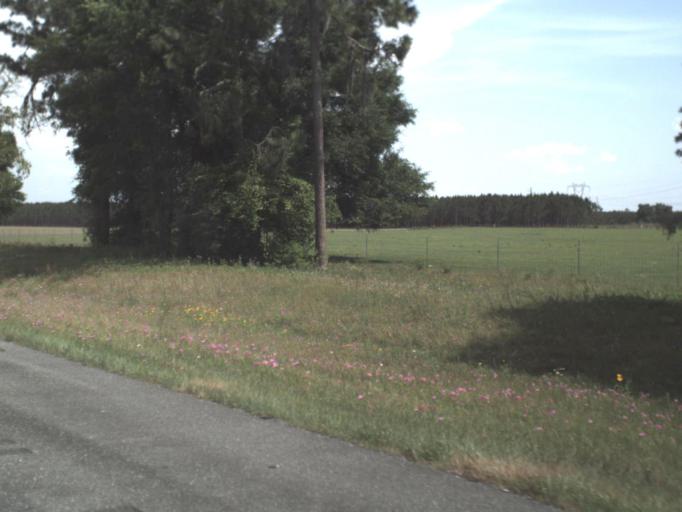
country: US
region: Florida
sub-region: Suwannee County
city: Live Oak
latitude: 30.3514
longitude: -83.1624
